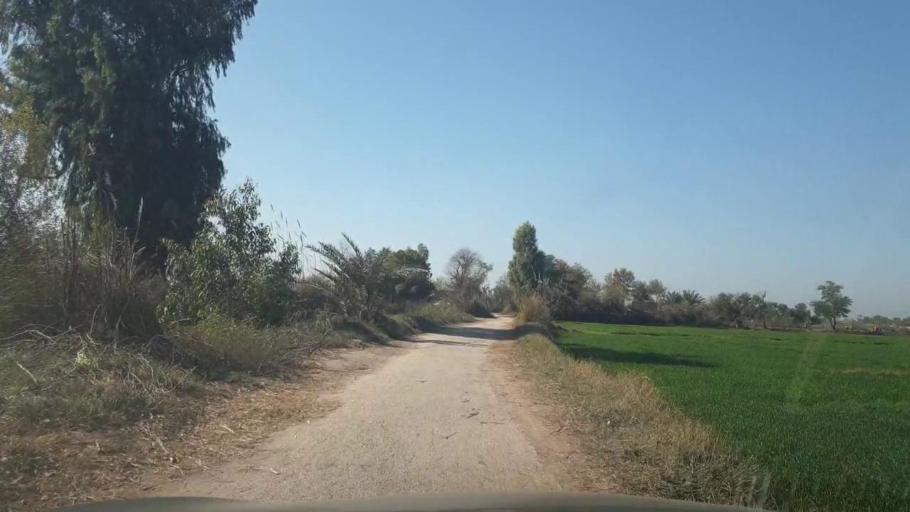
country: PK
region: Sindh
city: Mirpur Mathelo
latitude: 28.0612
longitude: 69.4966
